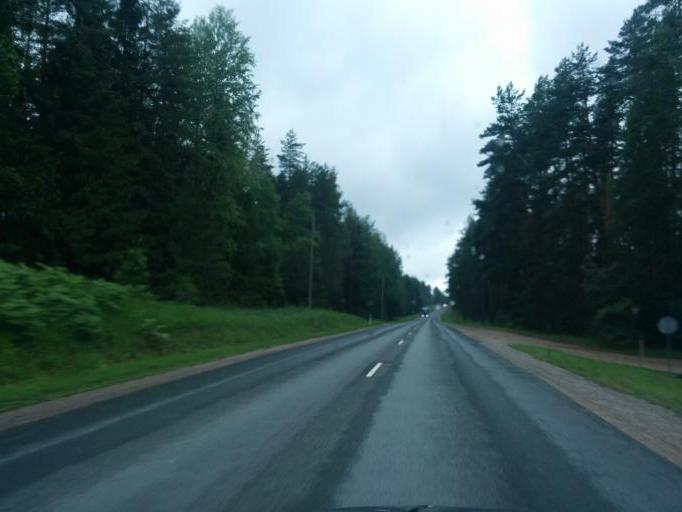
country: LV
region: Smiltene
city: Smiltene
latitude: 57.4042
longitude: 25.9509
